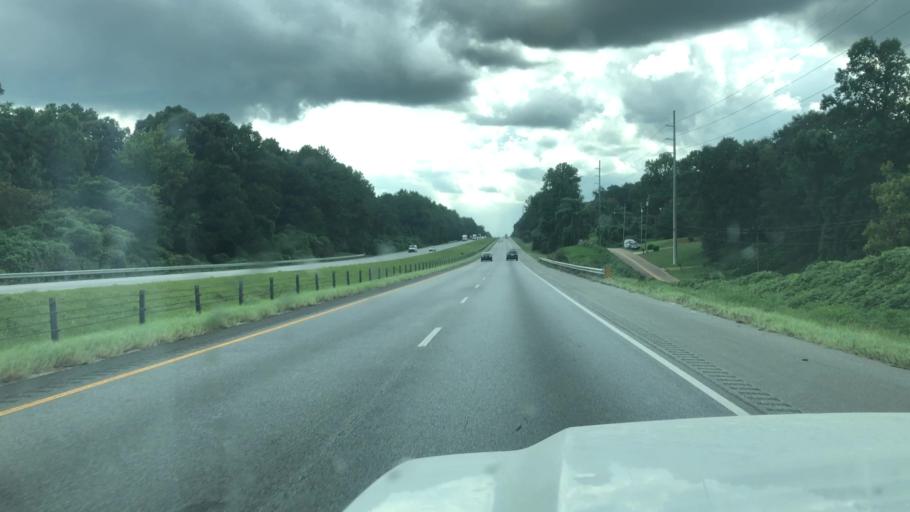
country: US
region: Alabama
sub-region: Lee County
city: Auburn
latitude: 32.5742
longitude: -85.4797
